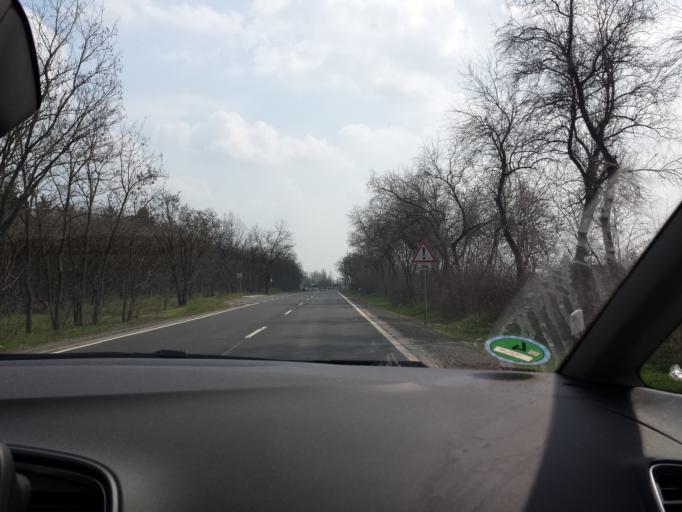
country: HU
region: Bacs-Kiskun
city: Nyarlorinc
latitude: 46.8726
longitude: 19.8528
